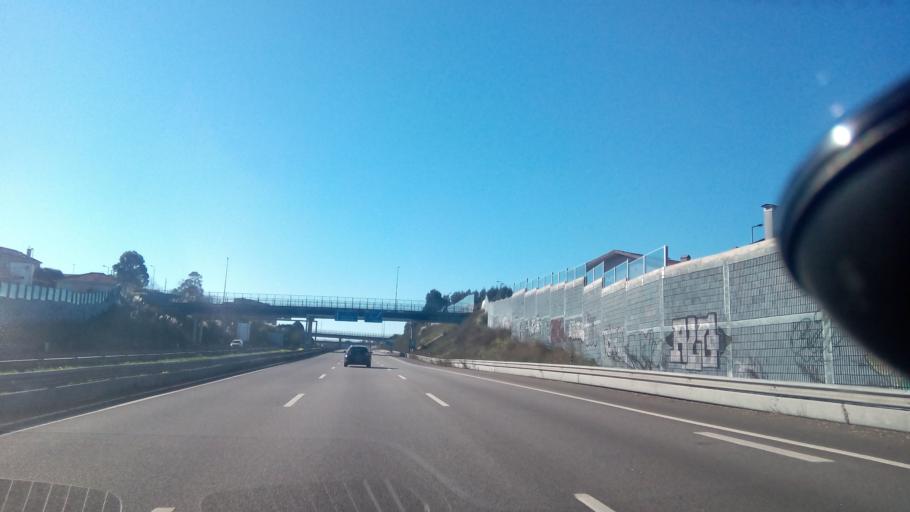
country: PT
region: Porto
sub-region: Matosinhos
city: Guifoes
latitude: 41.2009
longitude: -8.6579
